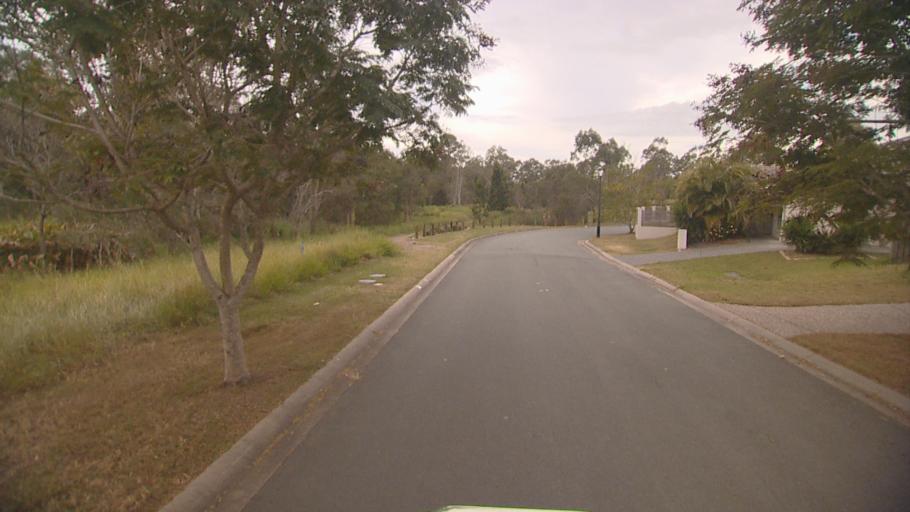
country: AU
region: Queensland
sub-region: Logan
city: Windaroo
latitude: -27.7186
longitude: 153.1709
